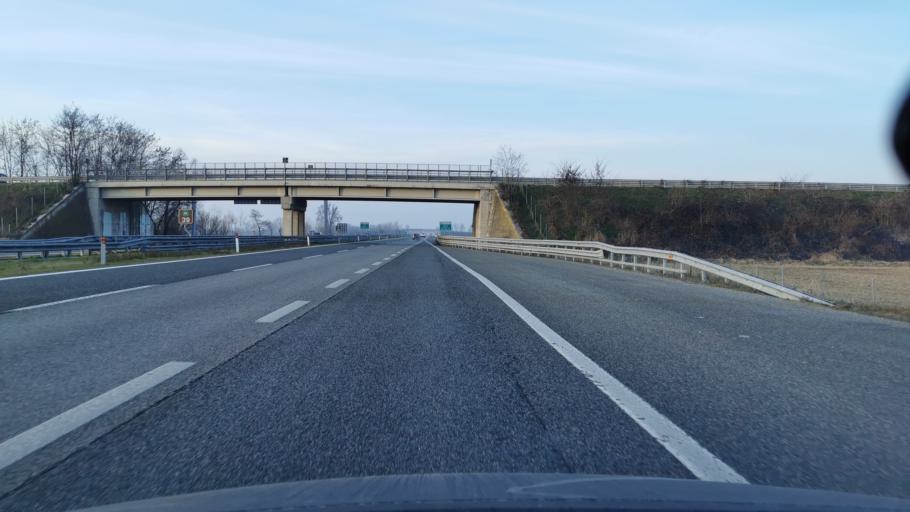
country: IT
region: Piedmont
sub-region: Provincia di Cuneo
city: Cervere
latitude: 44.6636
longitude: 7.7760
